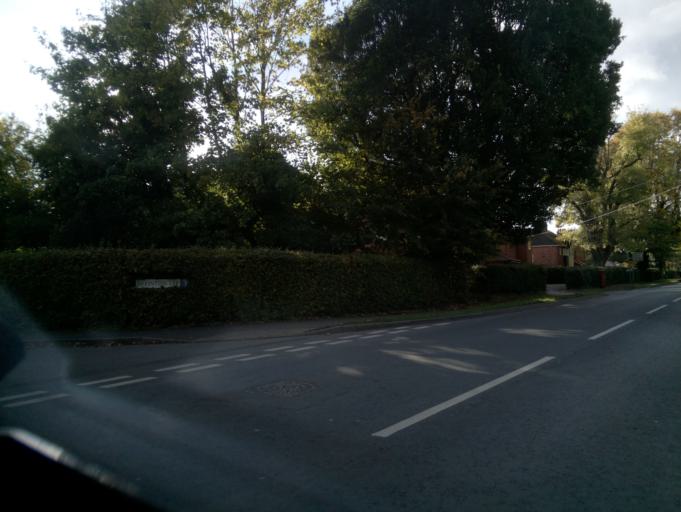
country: GB
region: England
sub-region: Herefordshire
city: Belmont
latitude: 52.0689
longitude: -2.7709
